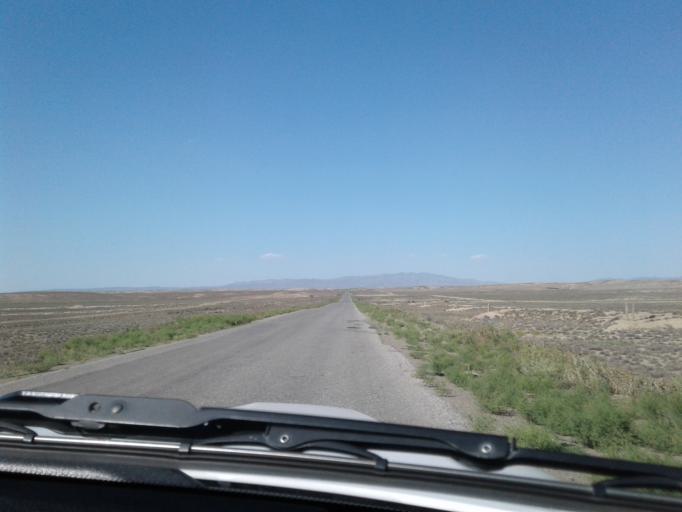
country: TM
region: Balkan
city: Magtymguly
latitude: 38.6177
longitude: 56.2253
